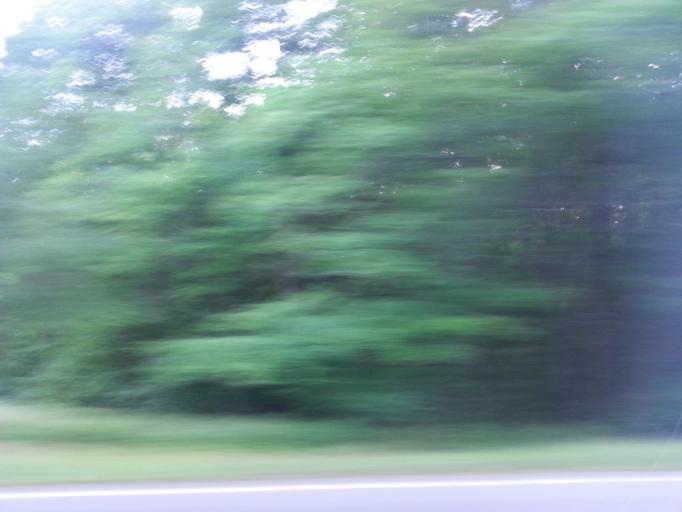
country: US
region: North Carolina
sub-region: Cherokee County
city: Murphy
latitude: 35.0374
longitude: -84.1428
